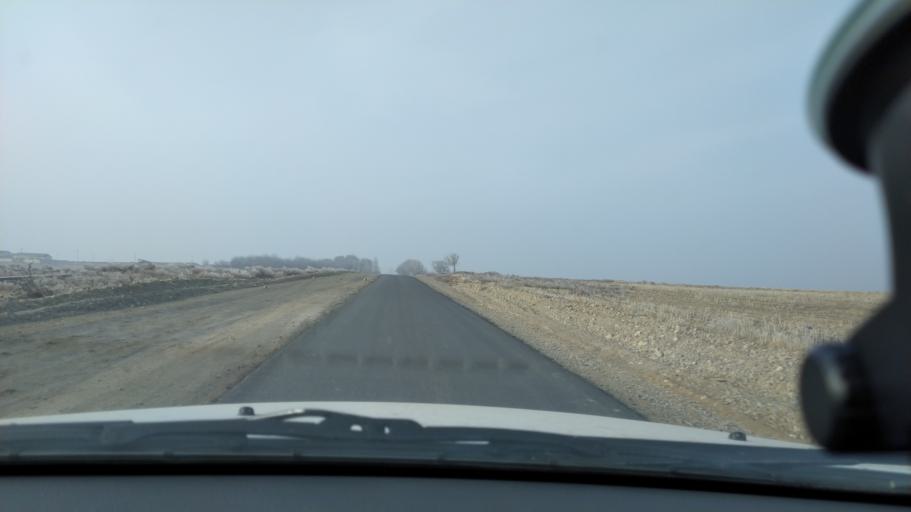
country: UZ
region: Namangan
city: Yangiqo`rg`on
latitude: 41.1354
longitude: 71.6487
